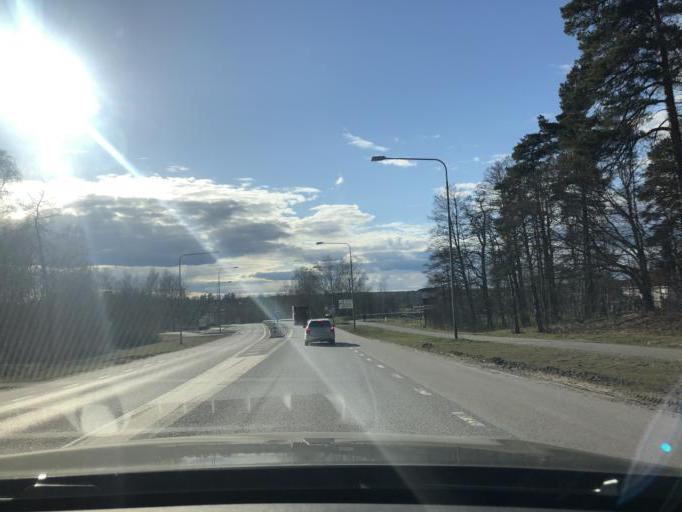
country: SE
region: Kalmar
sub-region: Vasterviks Kommun
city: Vaestervik
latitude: 57.7683
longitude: 16.5806
